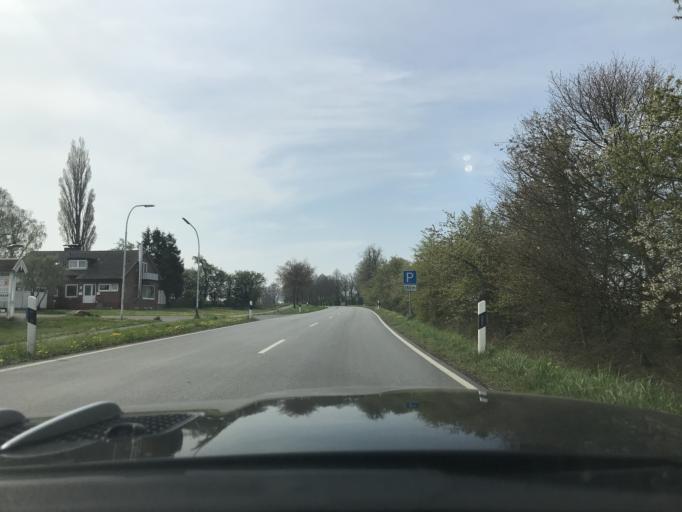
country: DE
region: Schleswig-Holstein
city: Grube
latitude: 54.2232
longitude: 11.0346
